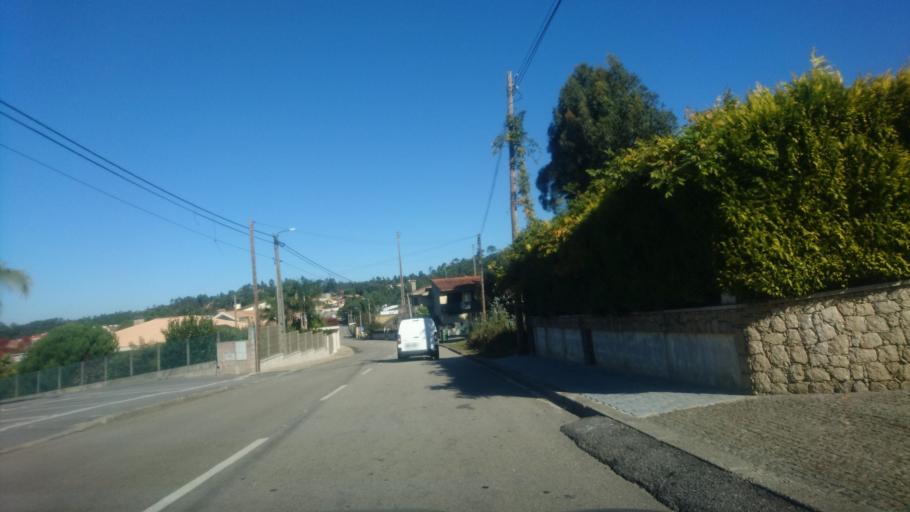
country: PT
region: Aveiro
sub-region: Oliveira de Azemeis
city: Sao Roque
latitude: 40.8768
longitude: -8.4648
